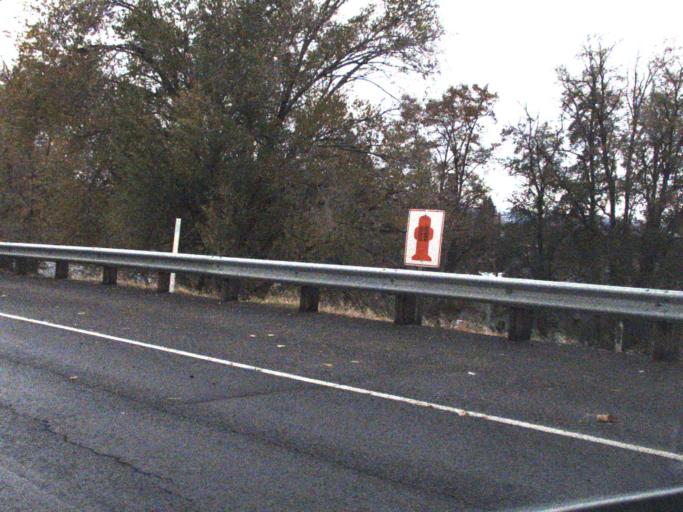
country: US
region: Washington
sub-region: Walla Walla County
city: Walla Walla
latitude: 46.0734
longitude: -118.3412
